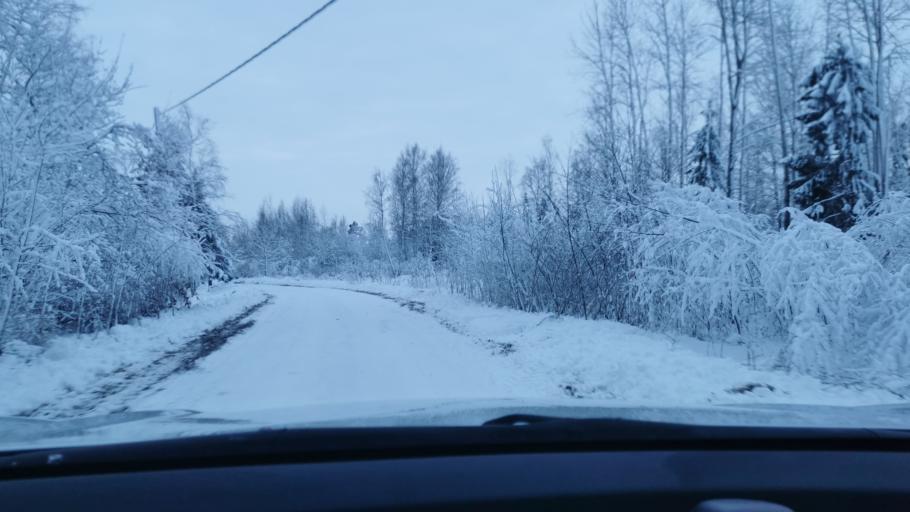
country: EE
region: Laeaene-Virumaa
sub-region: Someru vald
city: Someru
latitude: 59.4798
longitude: 26.4088
